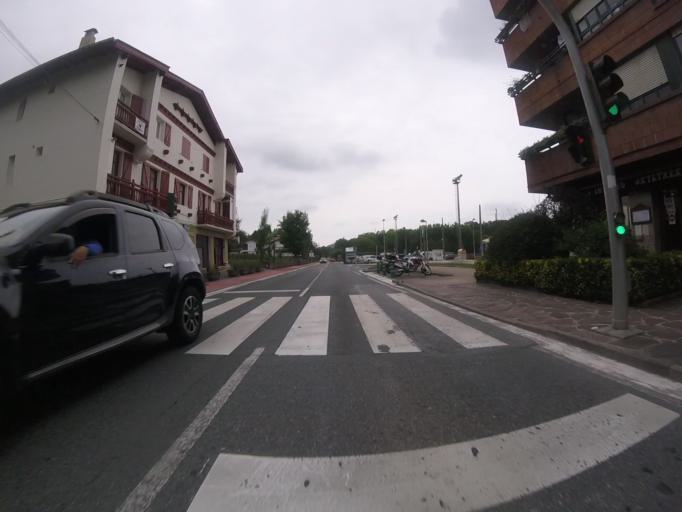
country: ES
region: Basque Country
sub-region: Provincia de Guipuzcoa
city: Errenteria
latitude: 43.2989
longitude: -1.8770
